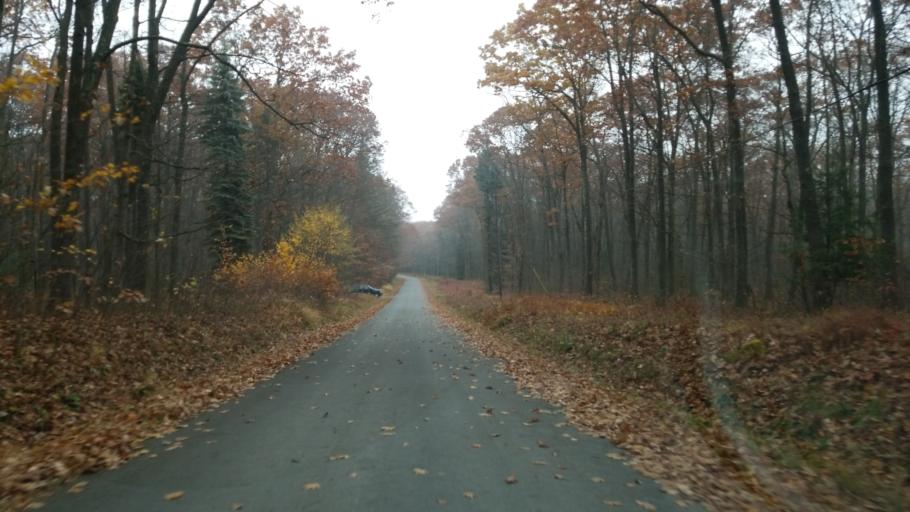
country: US
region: Pennsylvania
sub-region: Clearfield County
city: Clearfield
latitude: 41.1065
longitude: -78.5258
